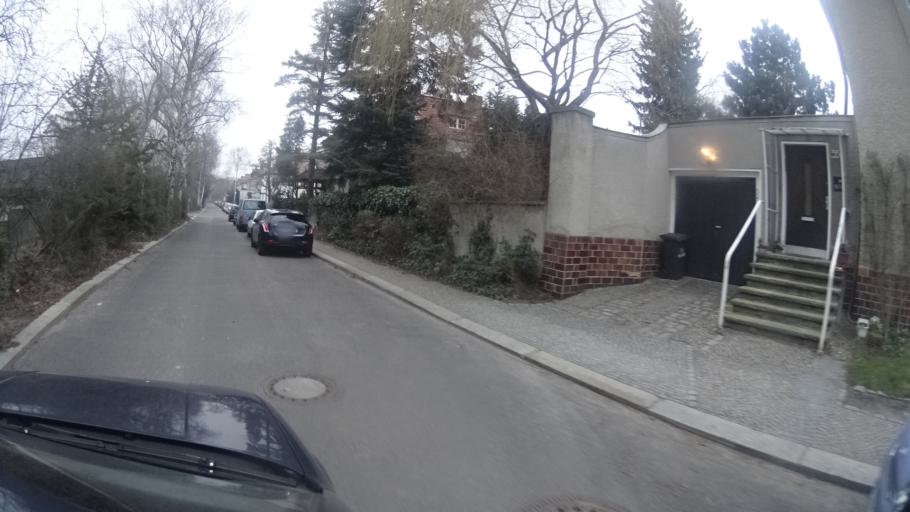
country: DE
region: Berlin
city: Tempelhof Bezirk
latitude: 52.4777
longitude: 13.3815
